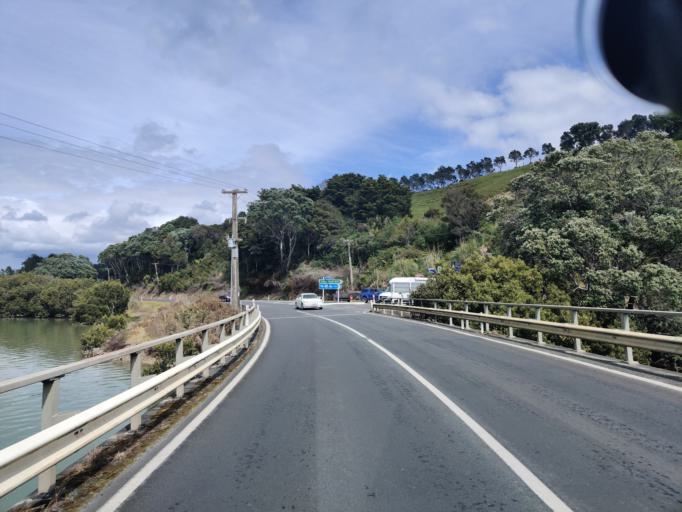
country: NZ
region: Northland
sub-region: Far North District
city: Taipa
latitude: -35.0555
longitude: 173.7002
